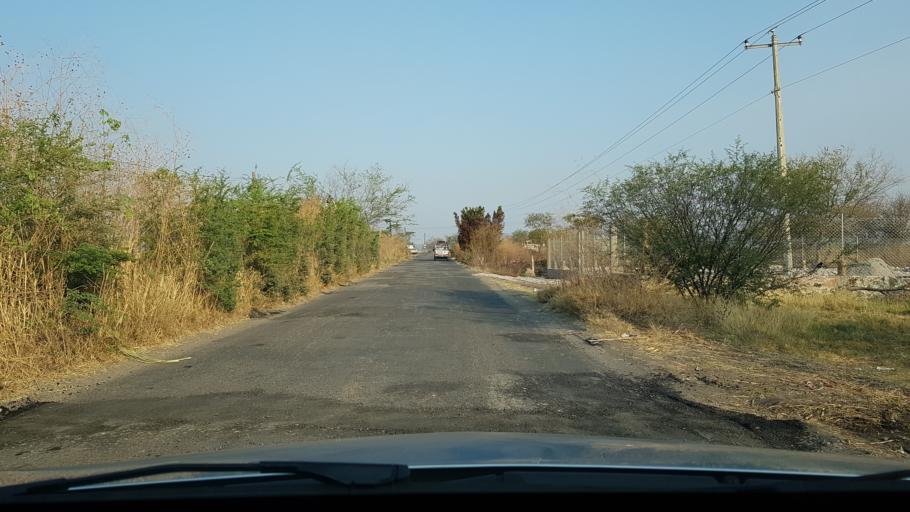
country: MX
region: Morelos
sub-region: Tepalcingo
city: Zacapalco
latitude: 18.6276
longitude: -99.0060
